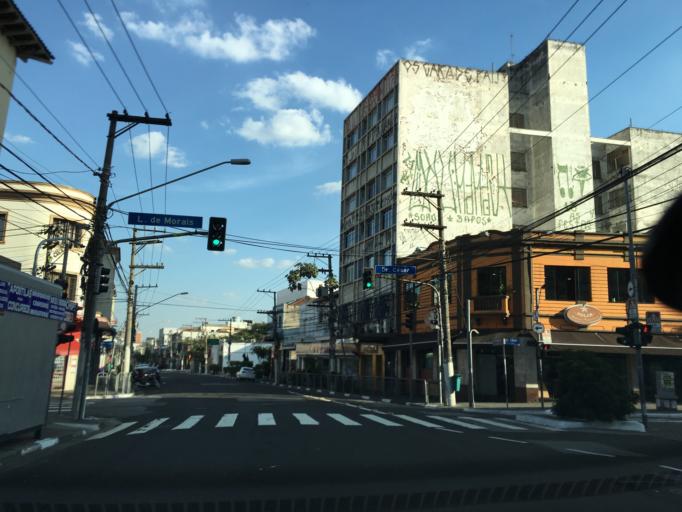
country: BR
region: Sao Paulo
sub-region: Sao Paulo
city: Sao Paulo
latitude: -23.5027
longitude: -46.6263
